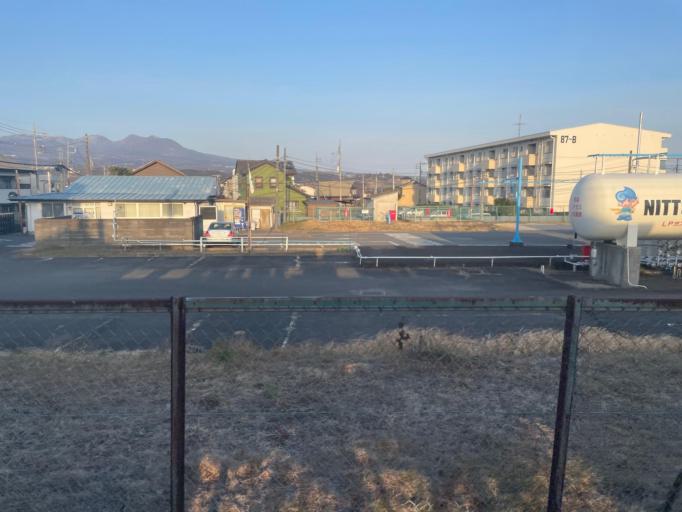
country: JP
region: Gunma
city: Shibukawa
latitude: 36.4614
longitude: 139.0198
